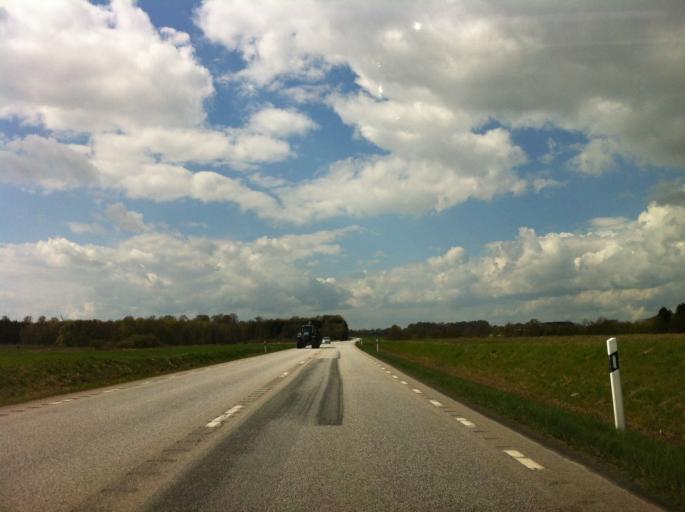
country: SE
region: Skane
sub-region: Hoors Kommun
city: Loberod
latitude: 55.8429
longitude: 13.4777
